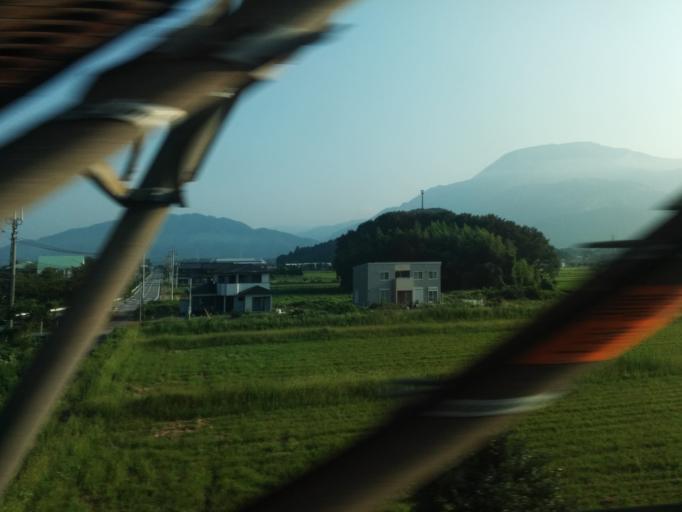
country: JP
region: Shiga Prefecture
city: Nagahama
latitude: 35.3674
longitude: 136.3687
